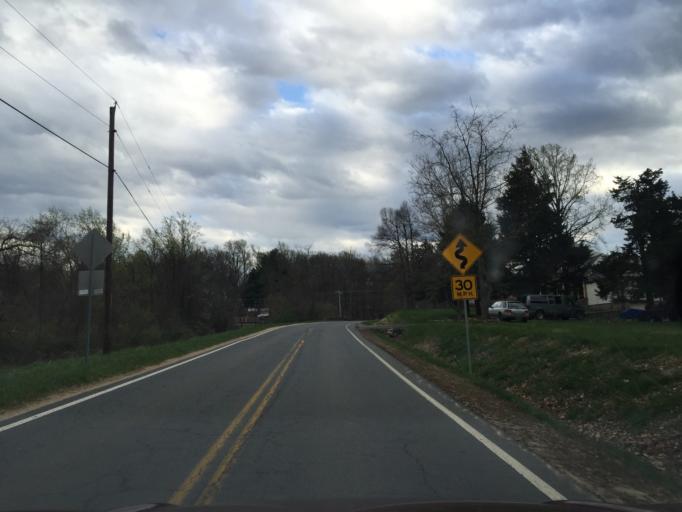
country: US
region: Maryland
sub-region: Frederick County
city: Point of Rocks
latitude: 39.2479
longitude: -77.5610
